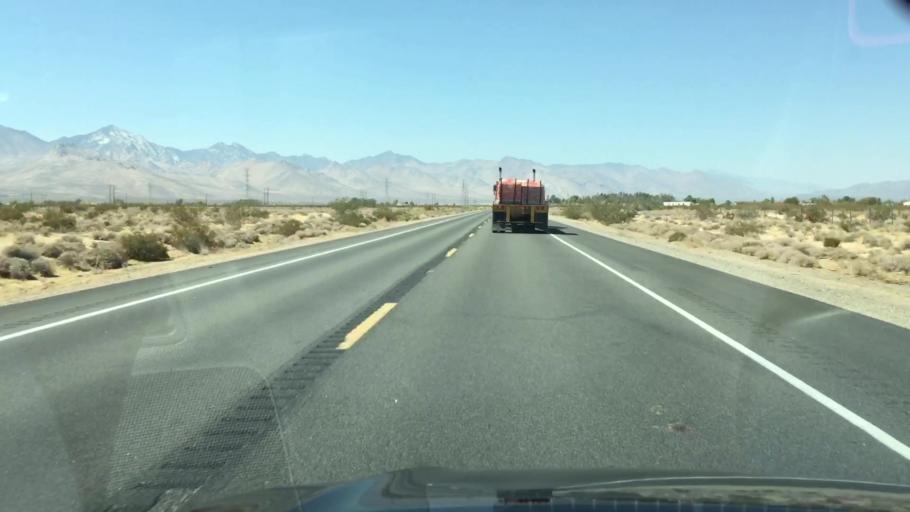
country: US
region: California
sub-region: Kern County
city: China Lake Acres
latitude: 35.6295
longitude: -117.7817
